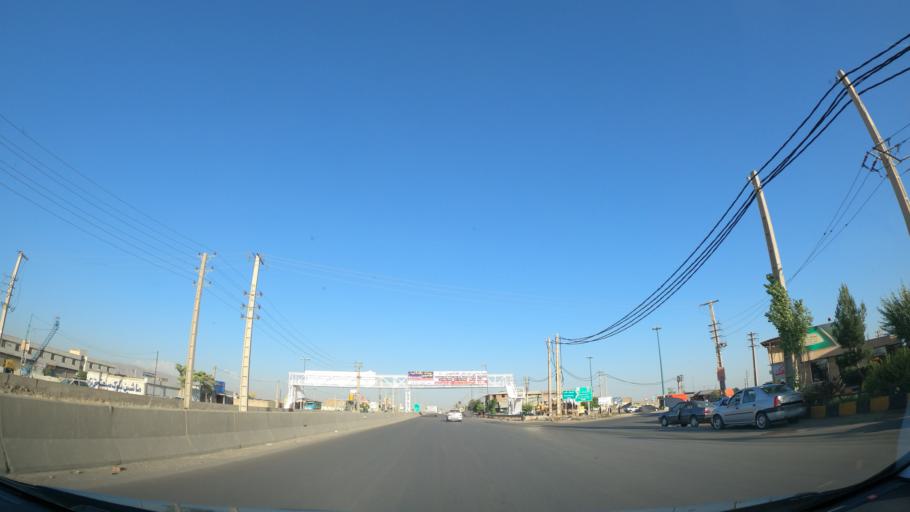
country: IR
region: Alborz
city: Hashtgerd
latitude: 35.9177
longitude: 50.7534
